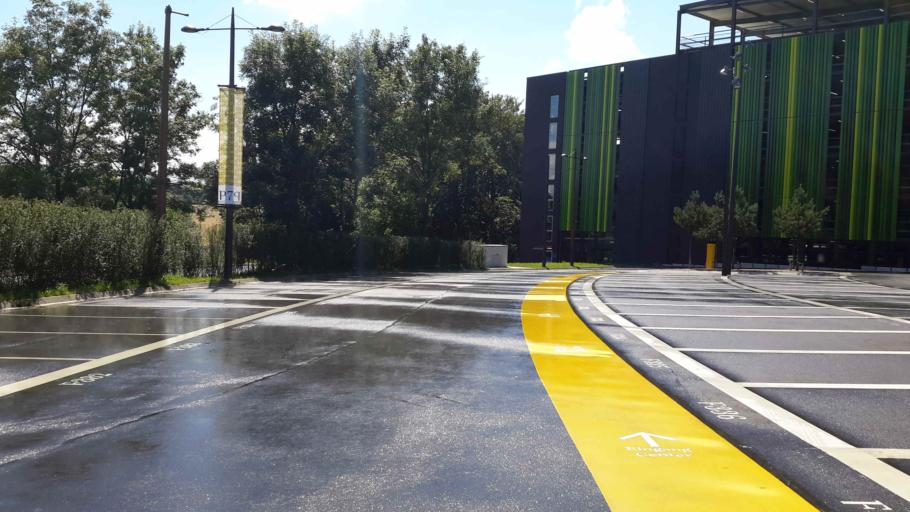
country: DE
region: North Rhine-Westphalia
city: Castrop-Rauxel
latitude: 51.4933
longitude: 7.2852
